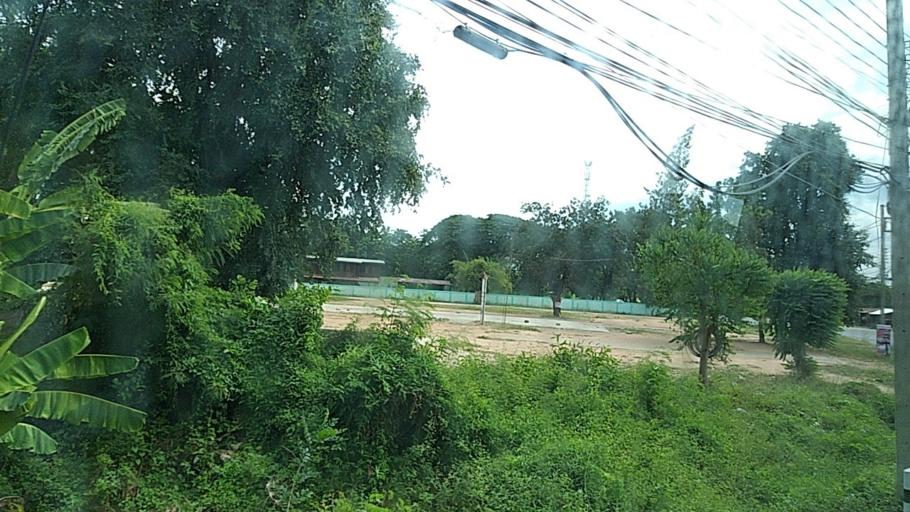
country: TH
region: Maha Sarakham
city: Chiang Yuen
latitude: 16.3460
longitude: 103.1236
